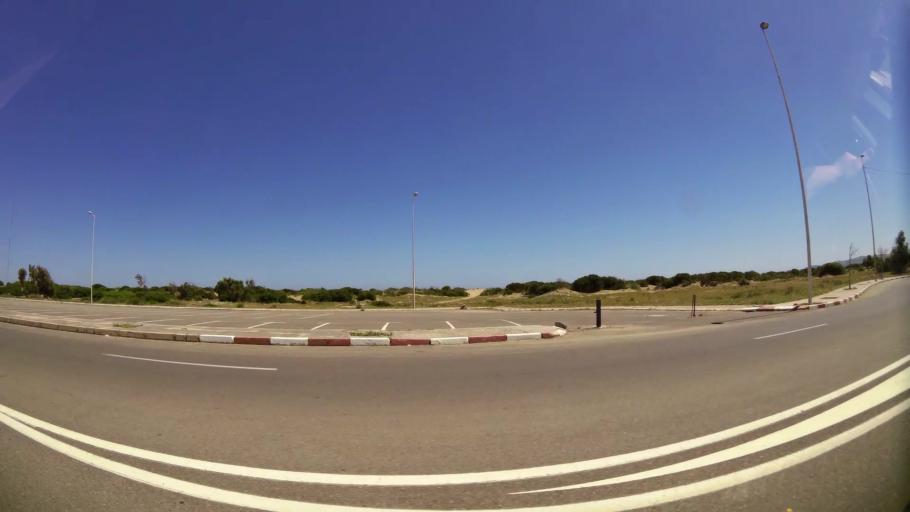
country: MA
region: Oriental
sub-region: Berkane-Taourirt
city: Madagh
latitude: 35.0945
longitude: -2.2597
